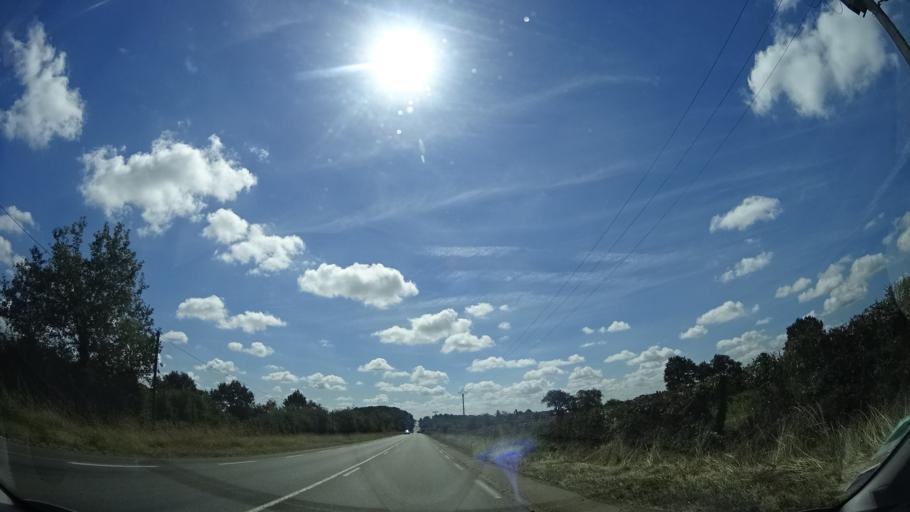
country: FR
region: Pays de la Loire
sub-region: Departement de la Sarthe
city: Auvers-le-Hamon
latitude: 47.8805
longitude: -0.4020
